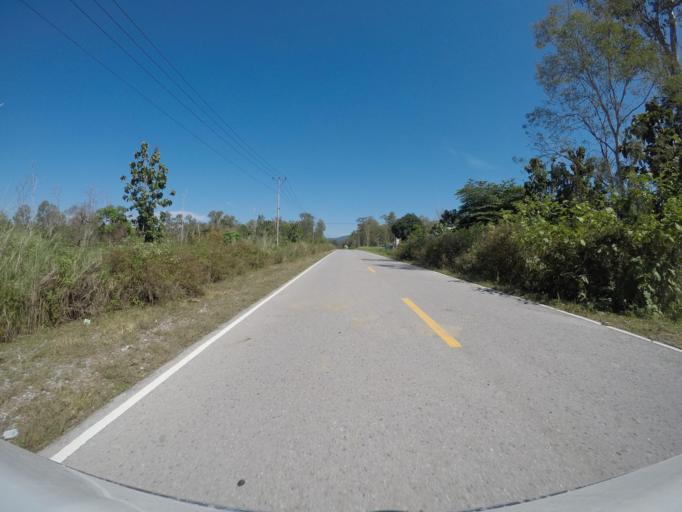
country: TL
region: Viqueque
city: Viqueque
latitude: -8.9679
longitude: 126.0258
